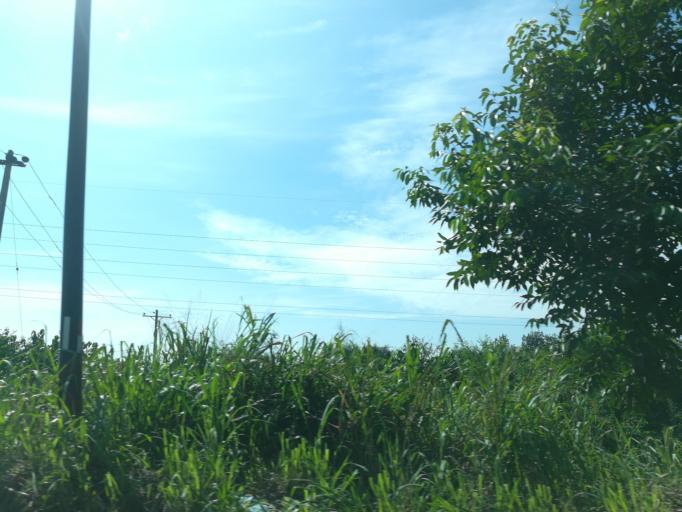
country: NG
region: Lagos
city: Ebute Ikorodu
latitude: 6.6189
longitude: 3.4490
